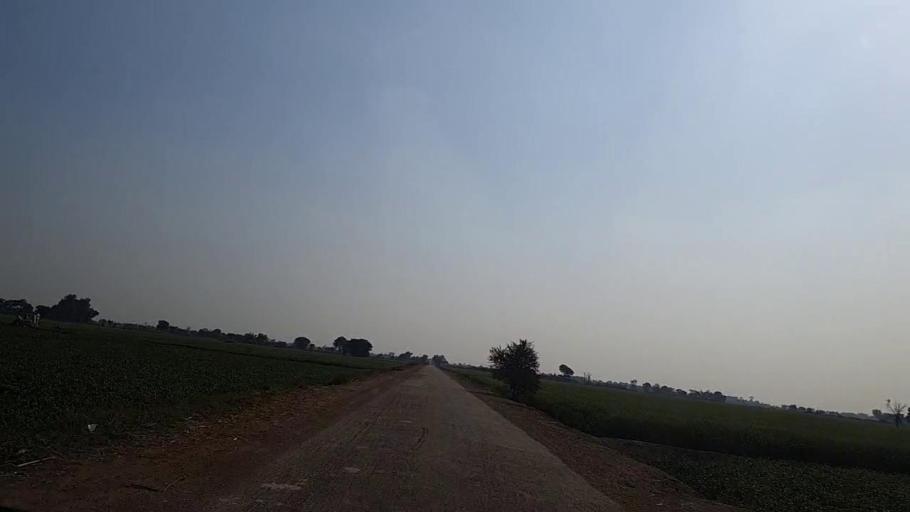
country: PK
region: Sindh
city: Sakrand
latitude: 26.0866
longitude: 68.2902
